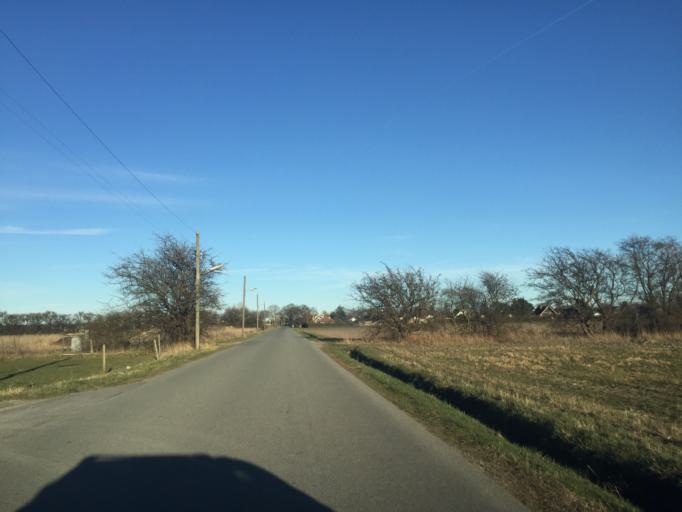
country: DK
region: Capital Region
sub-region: Dragor Kommune
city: Dragor
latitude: 55.6014
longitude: 12.6500
